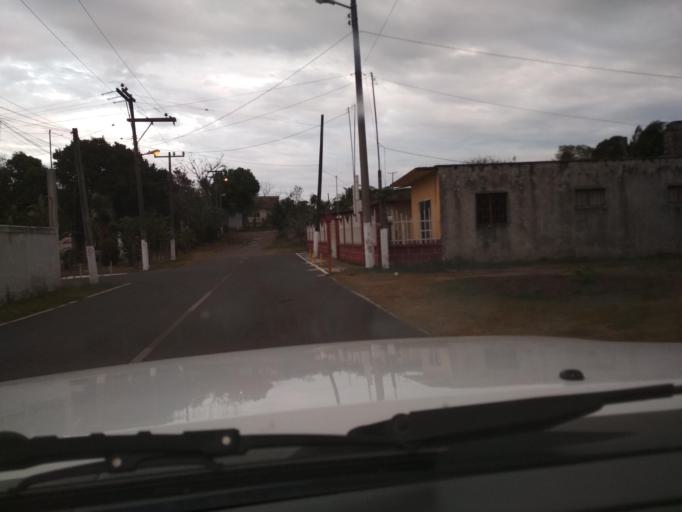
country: MX
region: Veracruz
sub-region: Veracruz
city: Delfino Victoria (Santa Fe)
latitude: 19.1607
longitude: -96.2607
